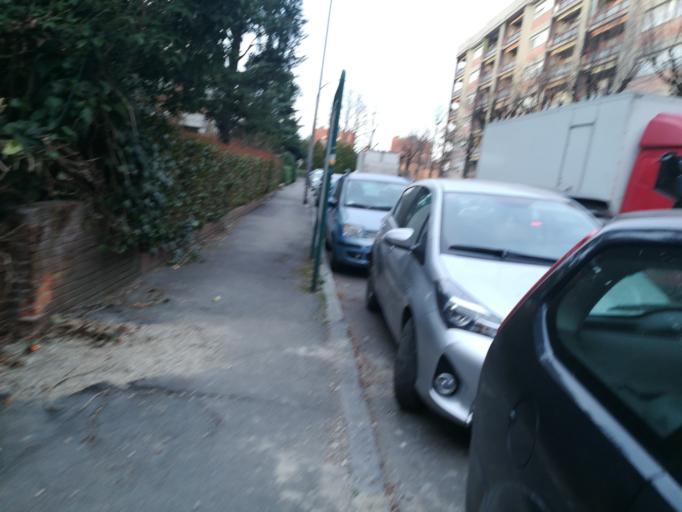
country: IT
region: Emilia-Romagna
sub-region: Provincia di Bologna
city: Progresso
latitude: 44.5473
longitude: 11.3594
